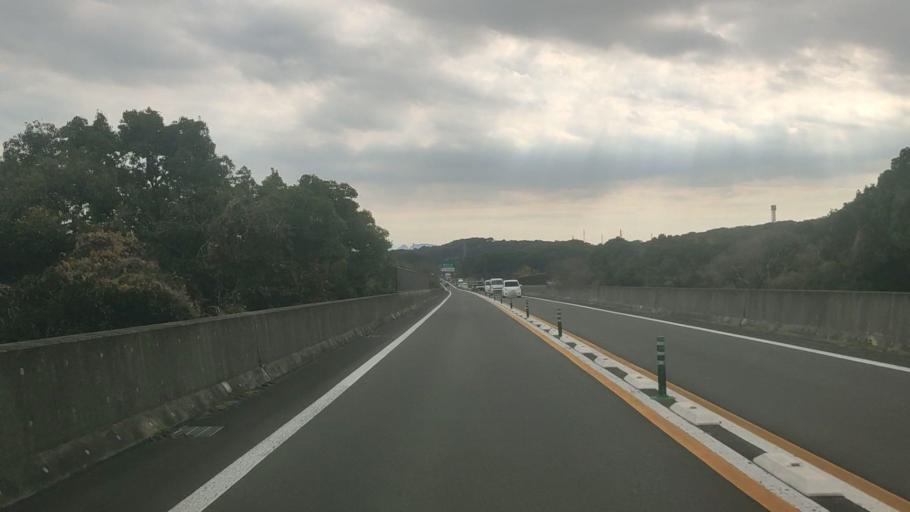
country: JP
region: Nagasaki
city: Shimabara
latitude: 32.7692
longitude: 130.3585
